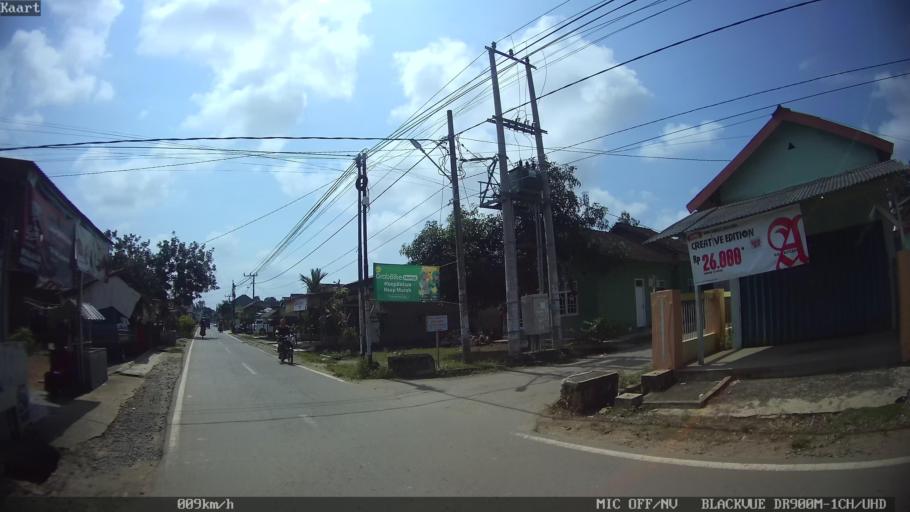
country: ID
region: Lampung
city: Kedaton
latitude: -5.3504
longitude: 105.2896
